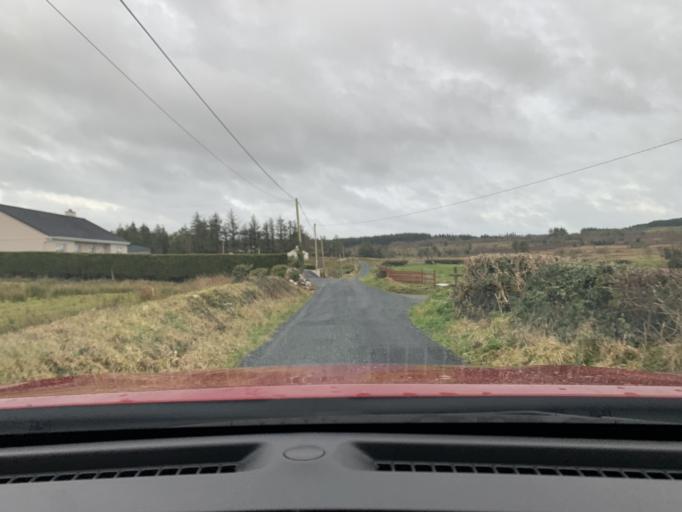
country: IE
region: Connaught
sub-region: Roscommon
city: Ballaghaderreen
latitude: 53.9678
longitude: -8.5173
